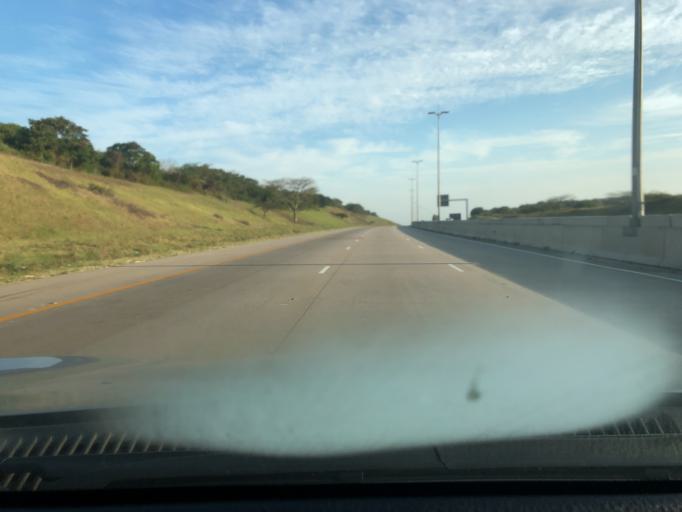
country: ZA
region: KwaZulu-Natal
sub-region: iLembe District Municipality
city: Ballitoville
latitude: -29.6070
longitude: 31.1366
